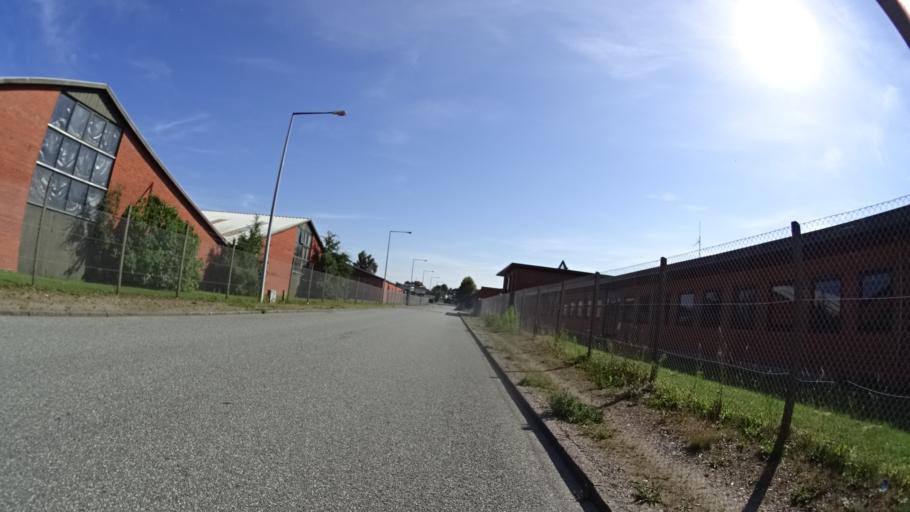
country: DK
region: Central Jutland
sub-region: Arhus Kommune
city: Stavtrup
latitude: 56.1441
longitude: 10.1475
